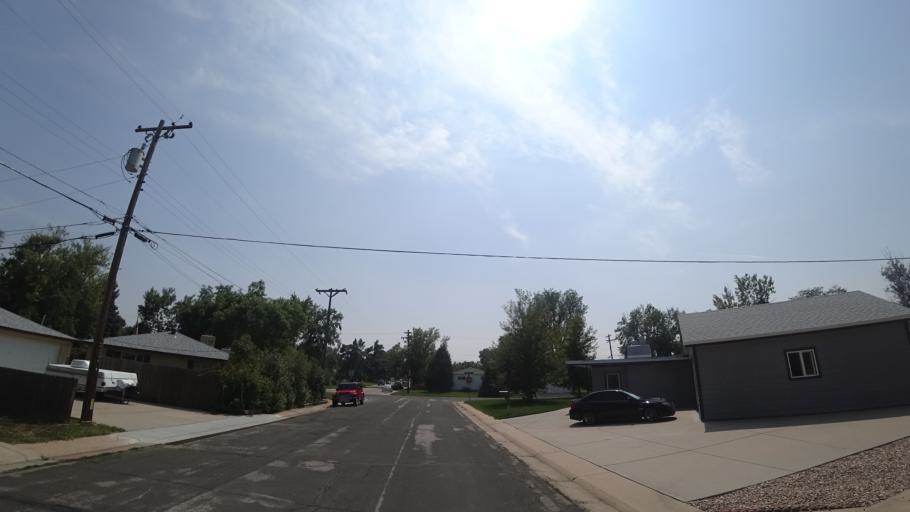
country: US
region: Colorado
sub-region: Arapahoe County
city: Englewood
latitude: 39.6354
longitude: -105.0008
